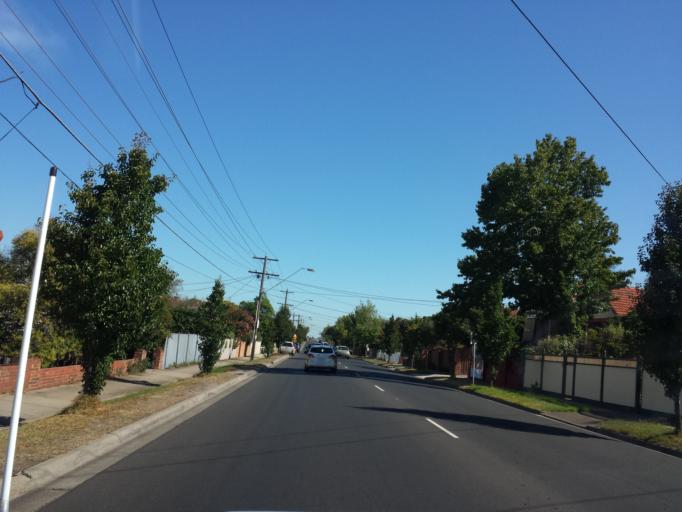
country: AU
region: Victoria
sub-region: Moonee Valley
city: Moonee Ponds
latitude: -37.7585
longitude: 144.9069
